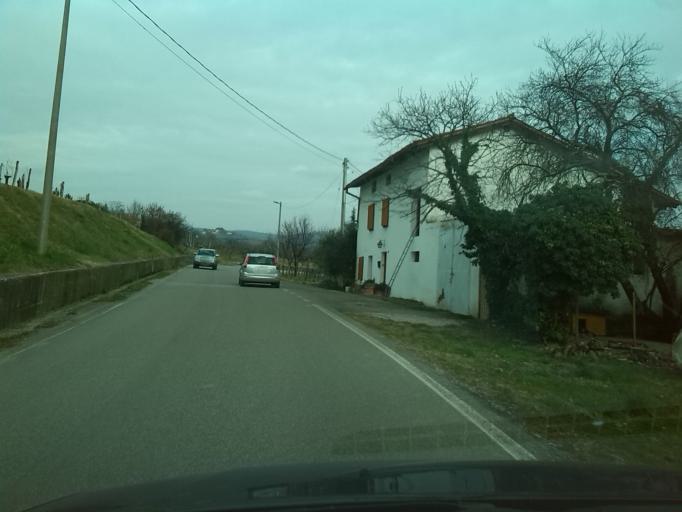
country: IT
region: Friuli Venezia Giulia
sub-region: Provincia di Gorizia
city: Mossa
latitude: 45.9661
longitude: 13.5540
